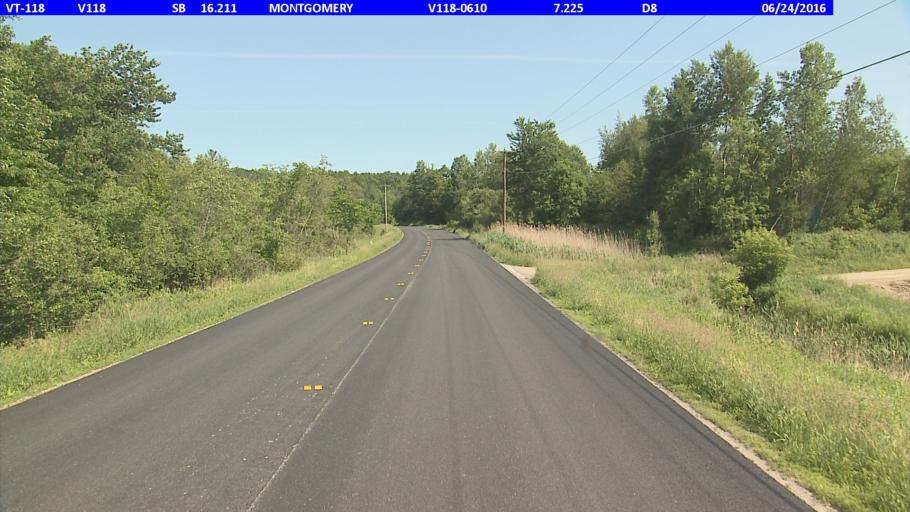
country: US
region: Vermont
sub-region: Franklin County
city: Richford
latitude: 44.8955
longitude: -72.6269
